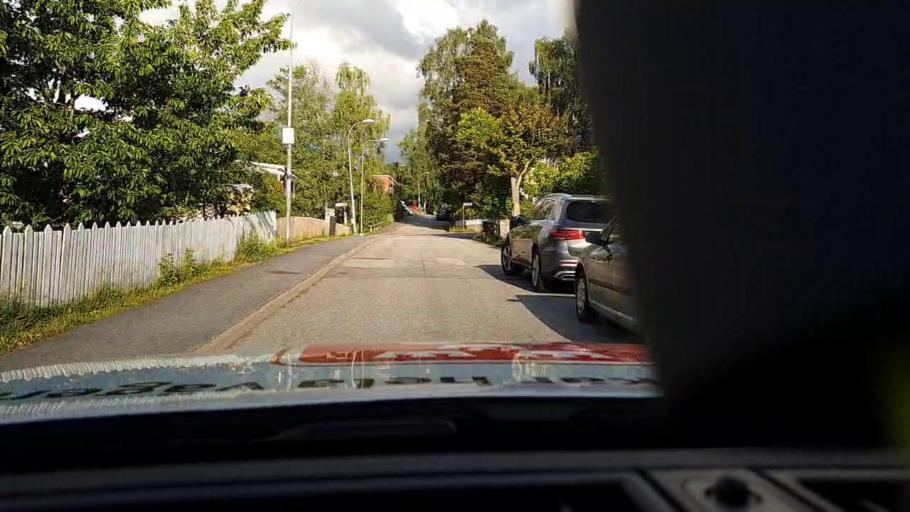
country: SE
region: Stockholm
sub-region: Huddinge Kommun
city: Huddinge
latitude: 59.2485
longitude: 17.9645
